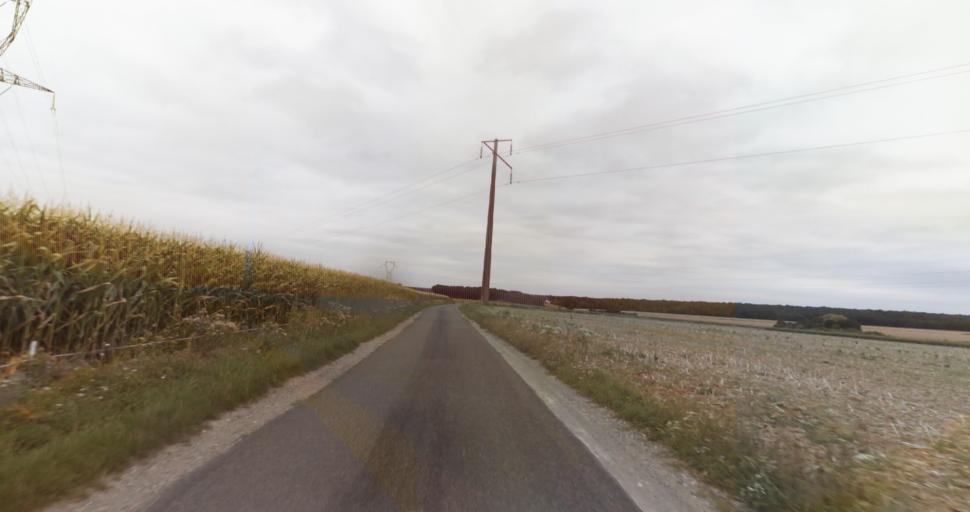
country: FR
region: Haute-Normandie
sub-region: Departement de l'Eure
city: Marcilly-sur-Eure
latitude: 48.8624
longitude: 1.3271
